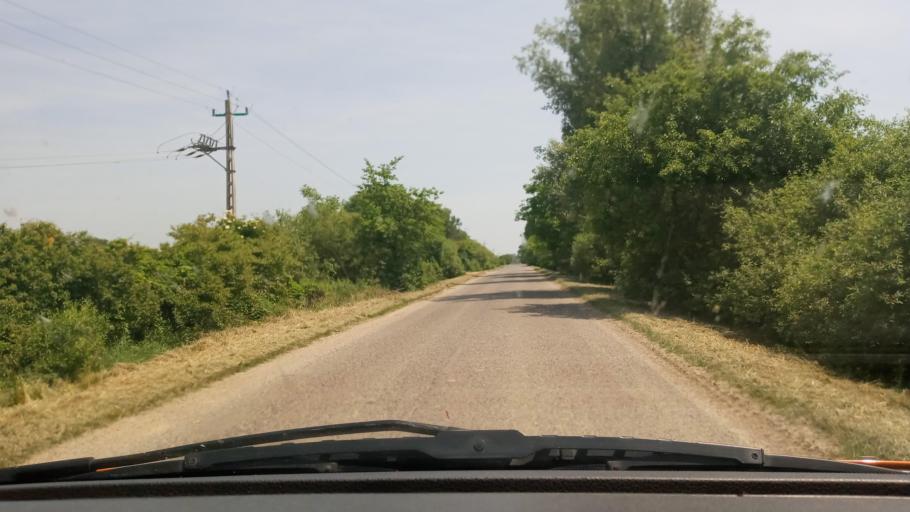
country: HU
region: Baranya
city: Szigetvar
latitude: 45.9658
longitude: 17.6969
